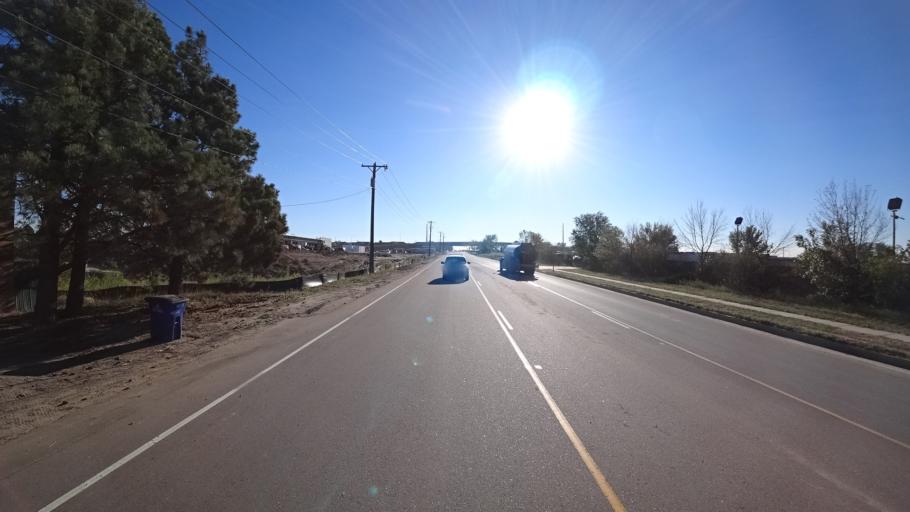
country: US
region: Colorado
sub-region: El Paso County
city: Stratmoor
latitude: 38.7817
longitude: -104.7618
